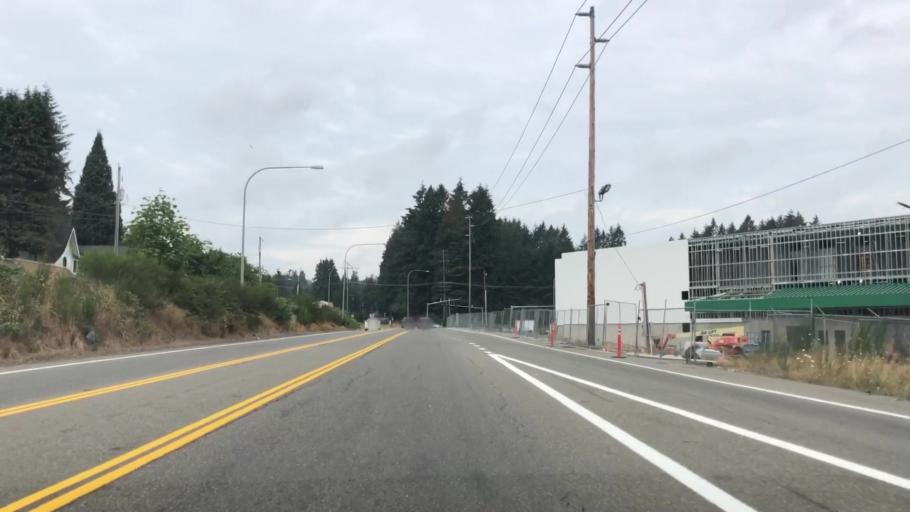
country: US
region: Washington
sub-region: Kitsap County
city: Navy Yard City
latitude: 47.5254
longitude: -122.7021
